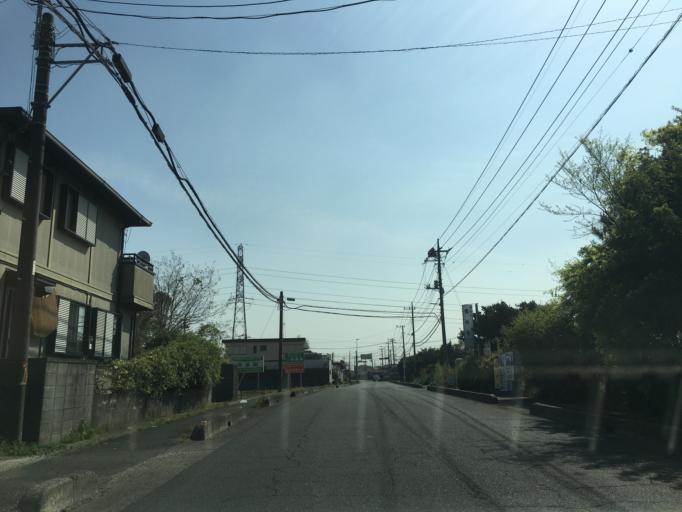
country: JP
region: Saitama
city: Sugito
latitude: 36.0108
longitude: 139.7221
